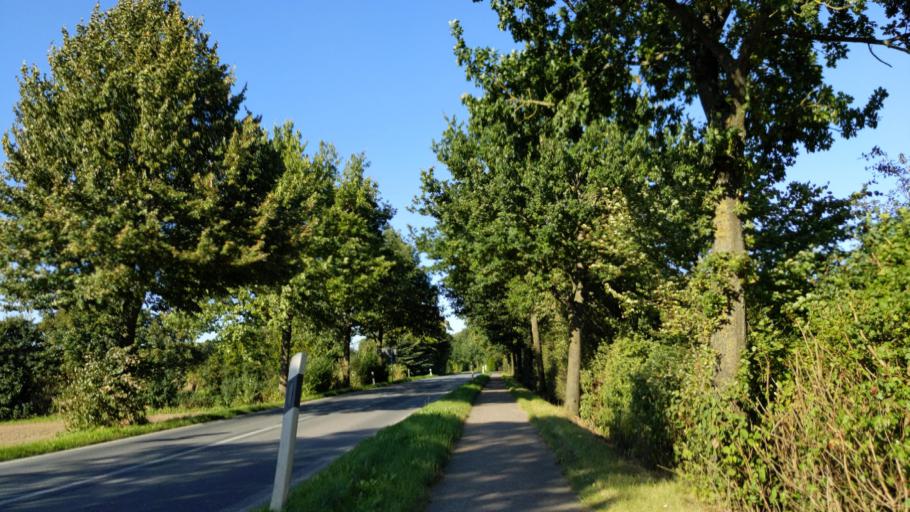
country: DE
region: Schleswig-Holstein
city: Ahrensbok
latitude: 53.9939
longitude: 10.5781
